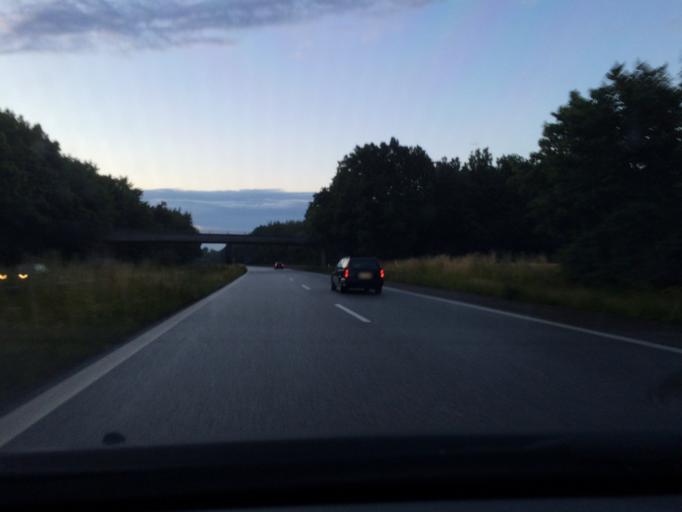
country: DK
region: Zealand
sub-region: Koge Kommune
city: Ejby
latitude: 55.4469
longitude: 12.1222
